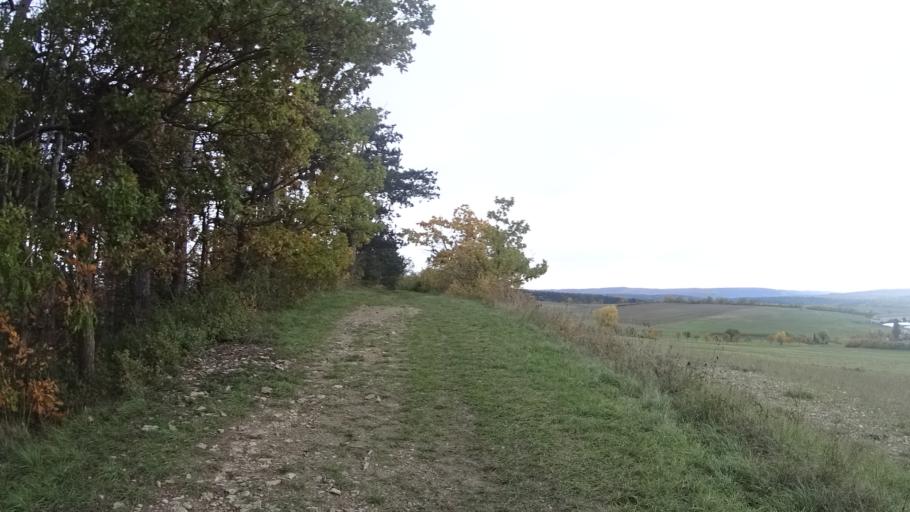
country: DE
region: Thuringia
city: Arnstadt
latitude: 50.8432
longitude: 10.8937
